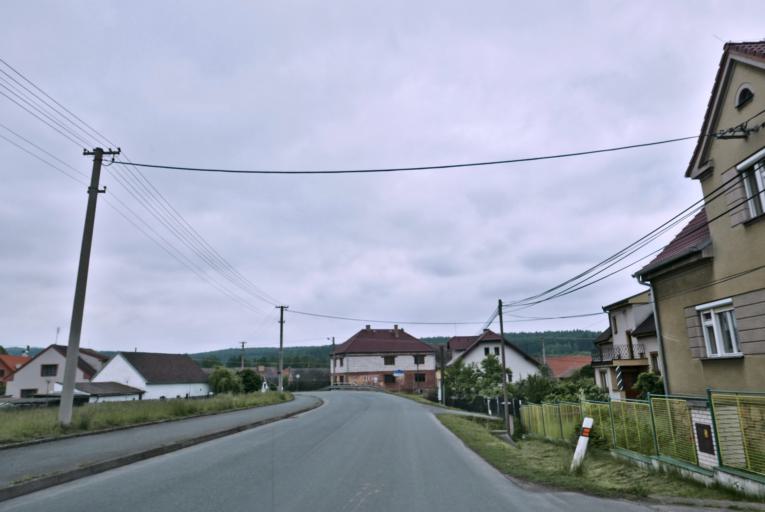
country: CZ
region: Plzensky
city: Plasy
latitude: 49.9865
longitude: 13.3612
